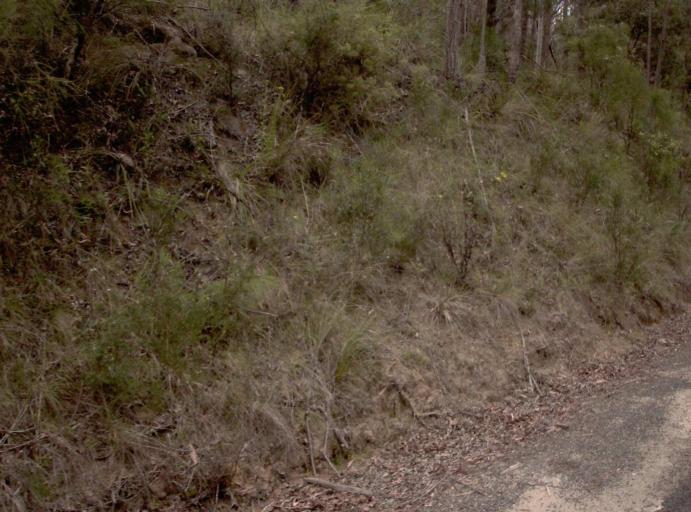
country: AU
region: New South Wales
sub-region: Bombala
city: Bombala
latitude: -37.3740
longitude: 149.2045
